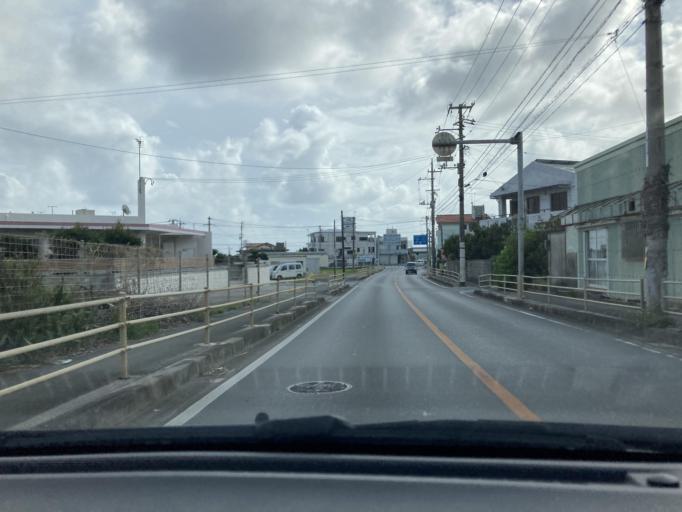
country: JP
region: Okinawa
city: Itoman
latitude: 26.0962
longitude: 127.6993
